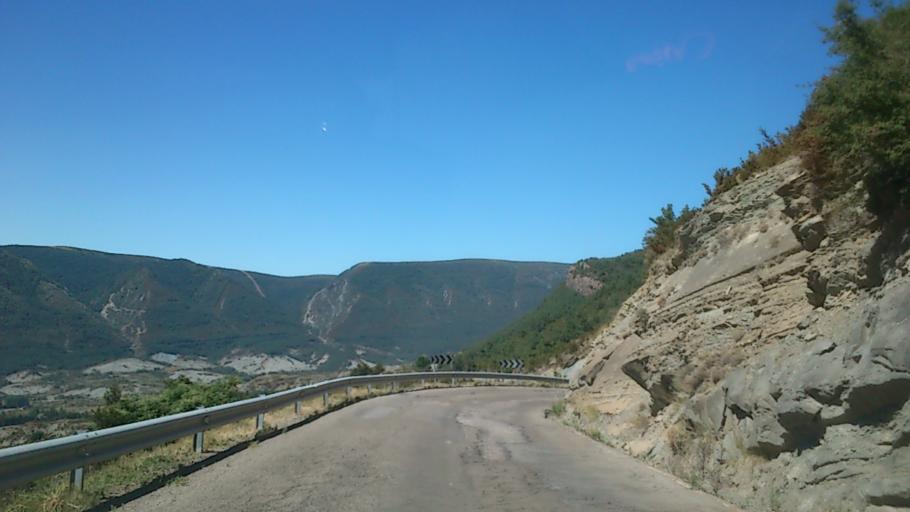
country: ES
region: Aragon
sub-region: Provincia de Huesca
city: Arguis
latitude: 42.3254
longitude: -0.4233
